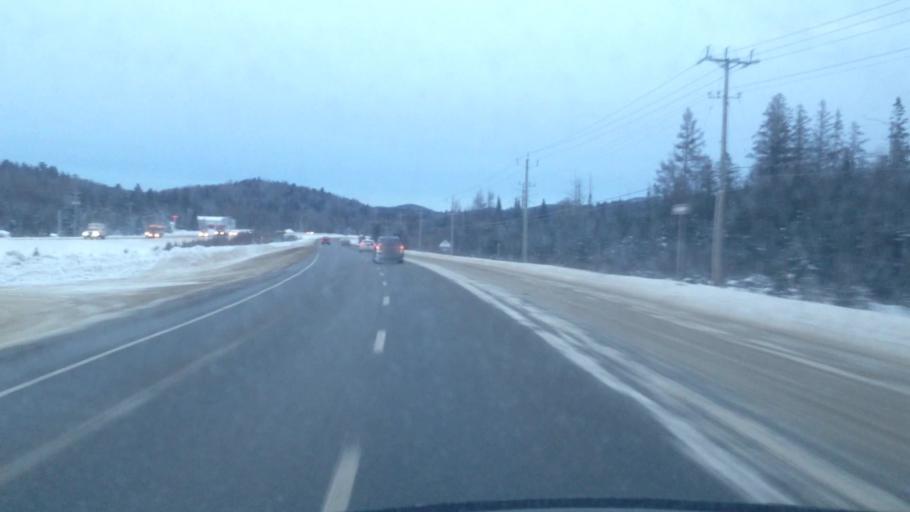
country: CA
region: Quebec
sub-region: Laurentides
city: Mont-Tremblant
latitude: 46.1119
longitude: -74.5287
